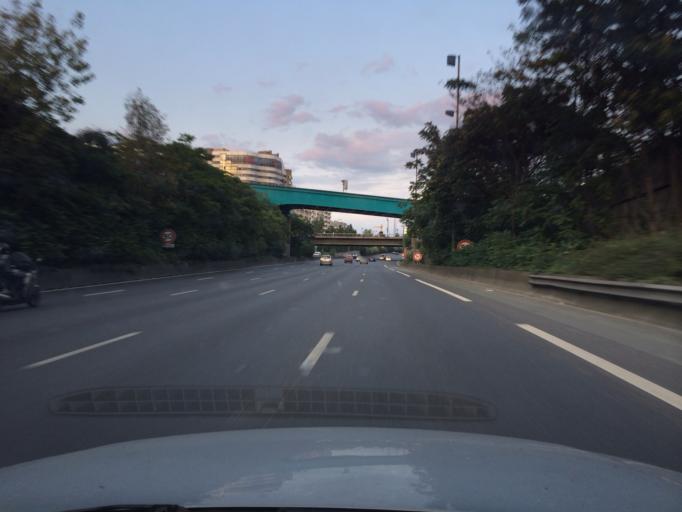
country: FR
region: Ile-de-France
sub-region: Departement du Val-de-Marne
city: Charenton-le-Pont
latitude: 48.8173
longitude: 2.4165
